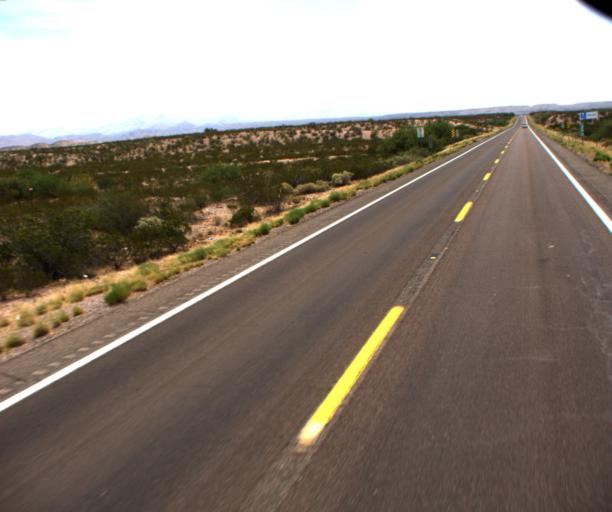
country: US
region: Arizona
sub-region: Graham County
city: Bylas
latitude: 33.1903
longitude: -110.1697
